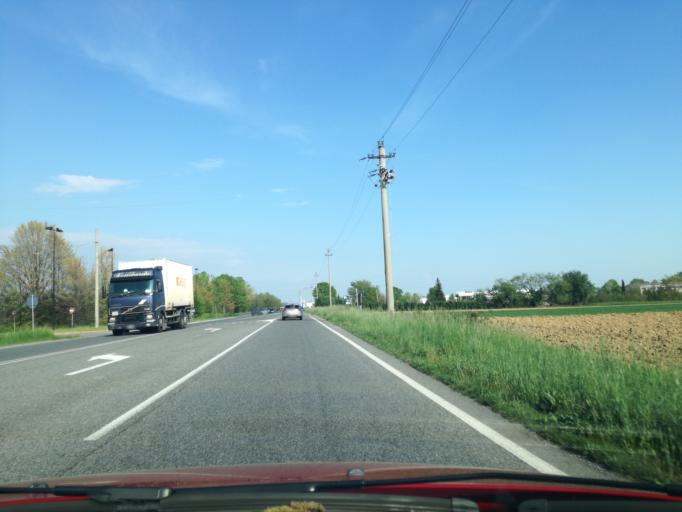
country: IT
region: Lombardy
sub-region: Provincia di Monza e Brianza
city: Bellusco
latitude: 45.6157
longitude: 9.4306
